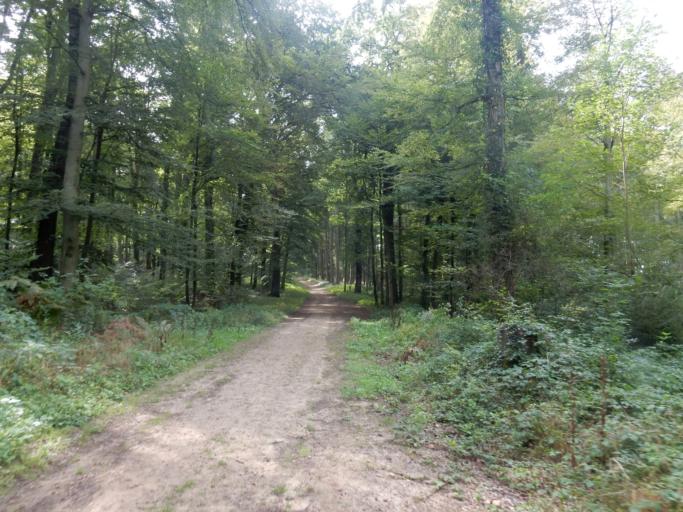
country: LU
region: Luxembourg
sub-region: Canton de Mersch
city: Mersch
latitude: 49.7285
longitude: 6.0903
